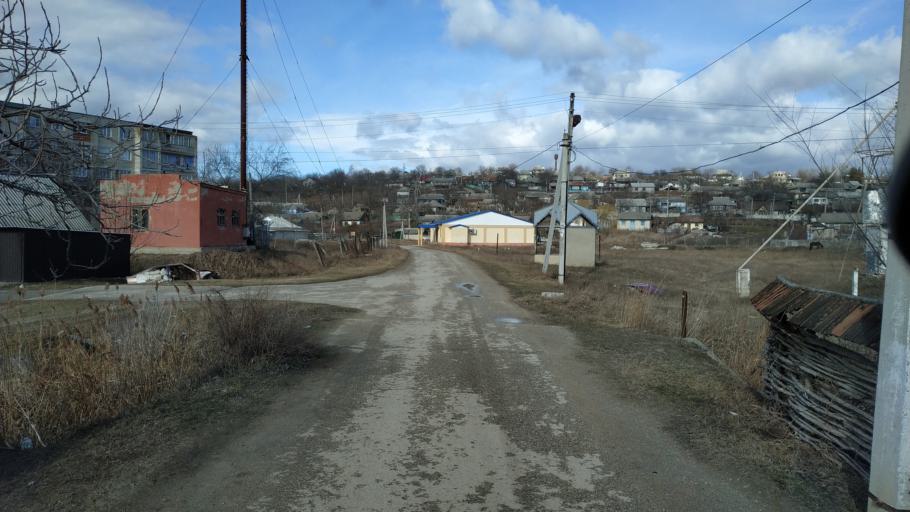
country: MD
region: Stinga Nistrului
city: Bucovat
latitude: 47.1856
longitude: 28.4713
